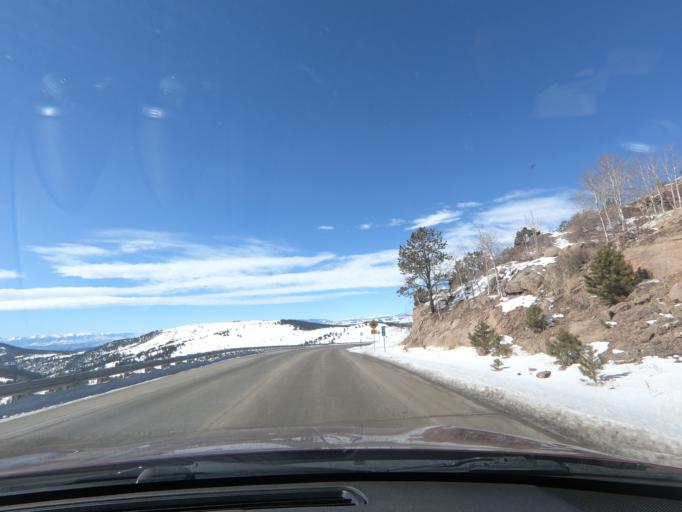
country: US
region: Colorado
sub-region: Teller County
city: Cripple Creek
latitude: 38.7102
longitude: -105.1489
